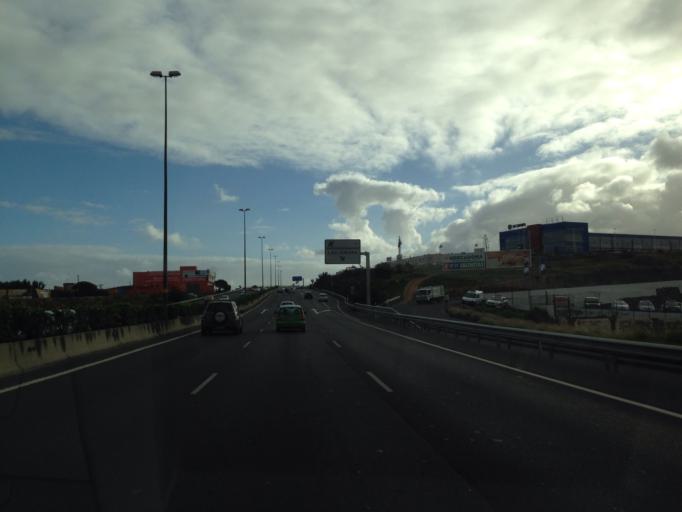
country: ES
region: Canary Islands
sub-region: Provincia de Las Palmas
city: Telde
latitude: 27.9902
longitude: -15.3923
